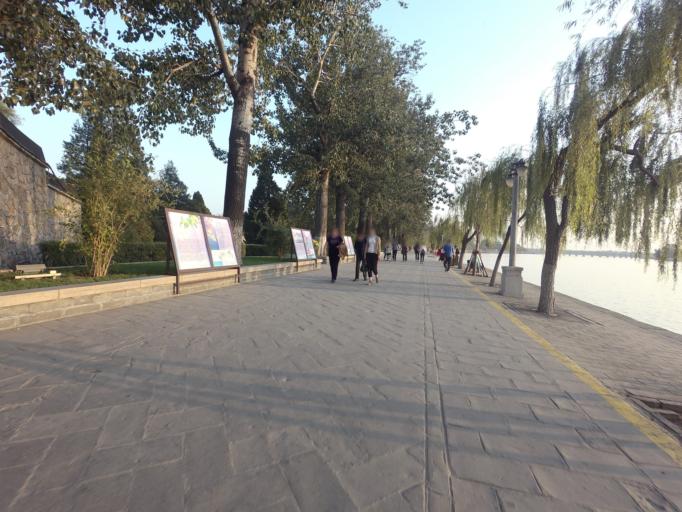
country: CN
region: Beijing
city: Haidian
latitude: 39.9944
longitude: 116.2743
